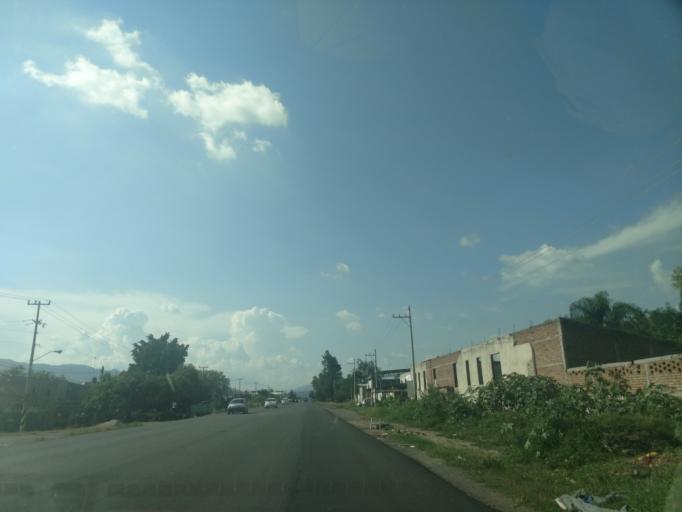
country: MX
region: Jalisco
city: Ahualulco de Mercado
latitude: 20.6992
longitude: -103.9652
